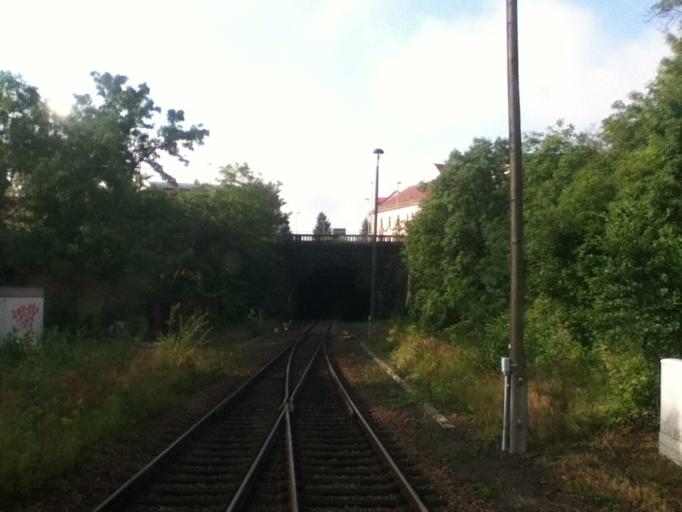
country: DE
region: Saxony
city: Kamenz
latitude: 51.2722
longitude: 14.0915
